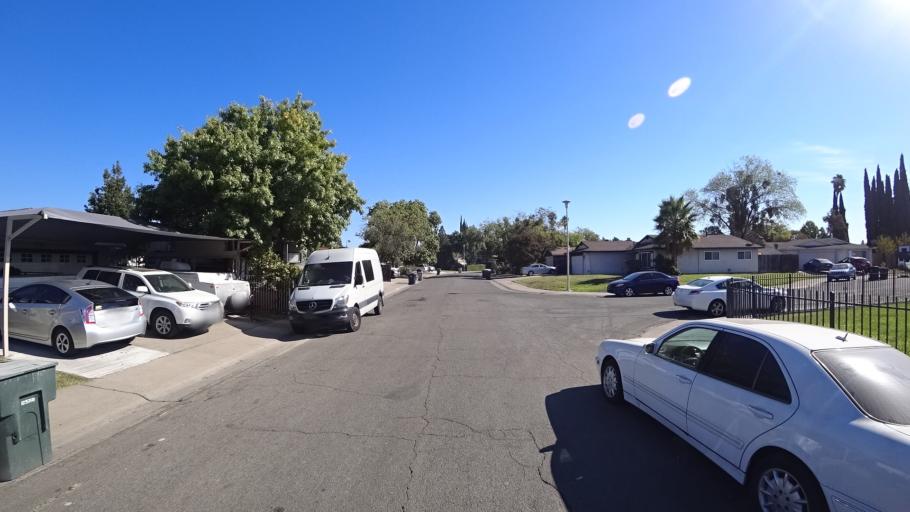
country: US
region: California
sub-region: Sacramento County
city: Florin
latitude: 38.4688
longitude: -121.4320
